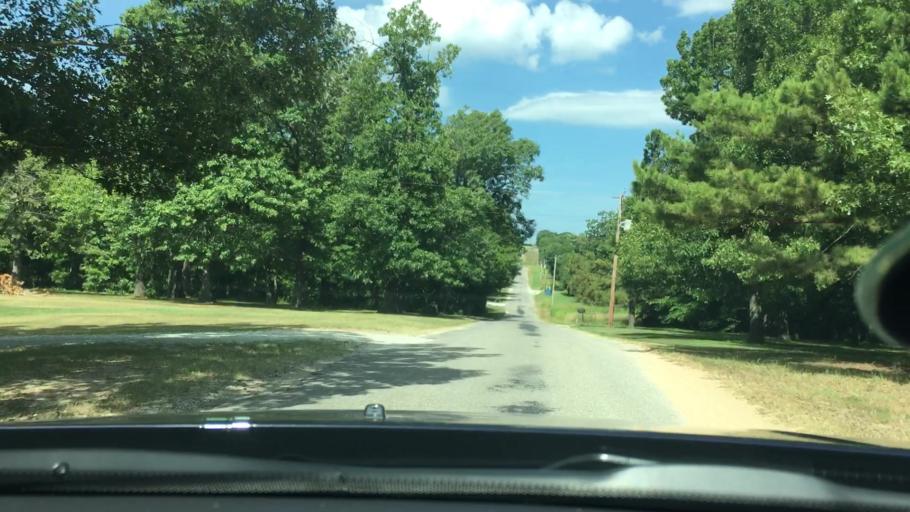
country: US
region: Oklahoma
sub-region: Pontotoc County
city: Ada
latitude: 34.7635
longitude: -96.5726
